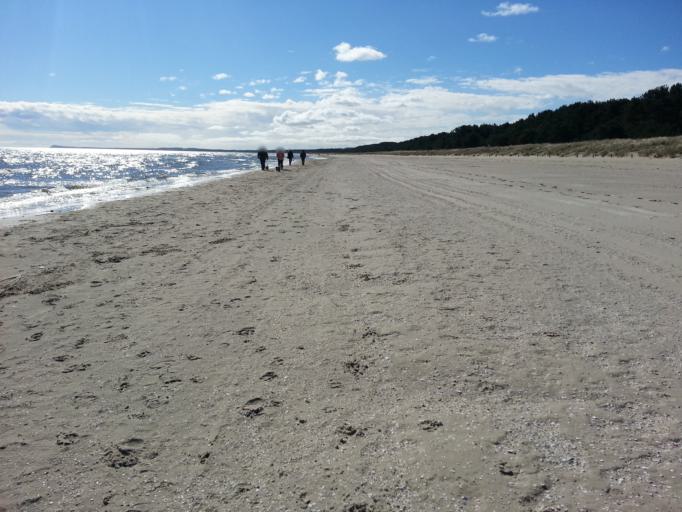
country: DE
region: Mecklenburg-Vorpommern
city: Karlshagen
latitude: 54.1356
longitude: 13.8304
